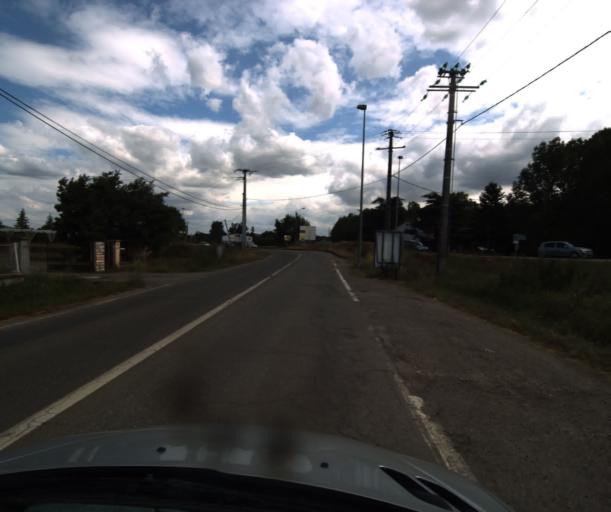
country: FR
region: Midi-Pyrenees
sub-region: Departement du Tarn-et-Garonne
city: Montauban
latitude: 43.9963
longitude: 1.3500
